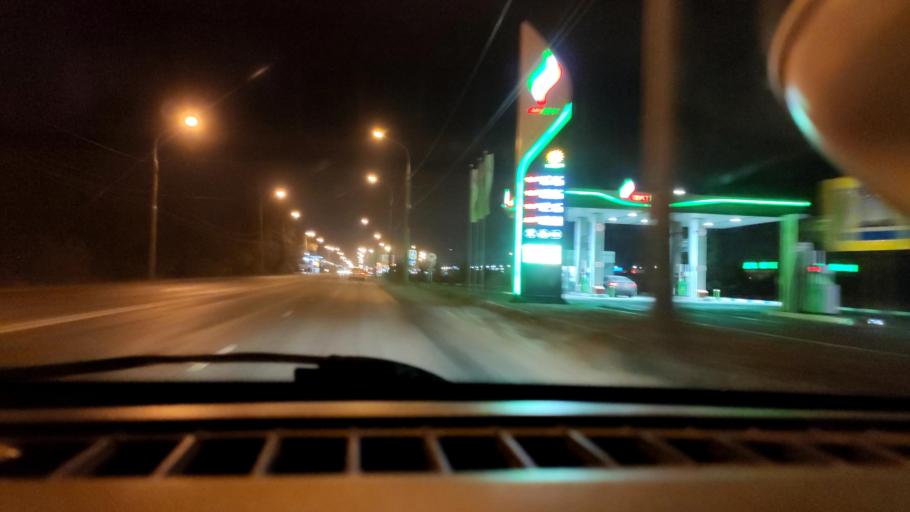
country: RU
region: Samara
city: Samara
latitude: 53.1455
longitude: 50.1826
